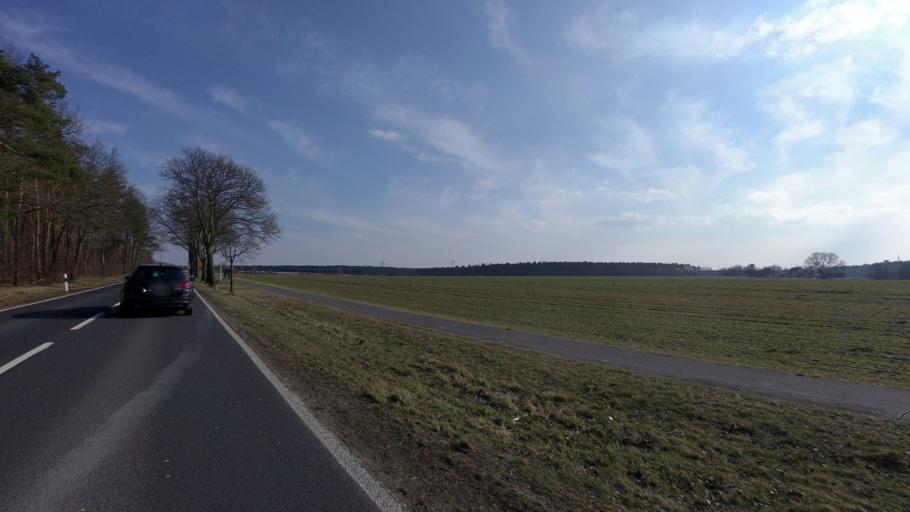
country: DE
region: Brandenburg
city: Ludwigsfelde
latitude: 52.2909
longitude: 13.2755
